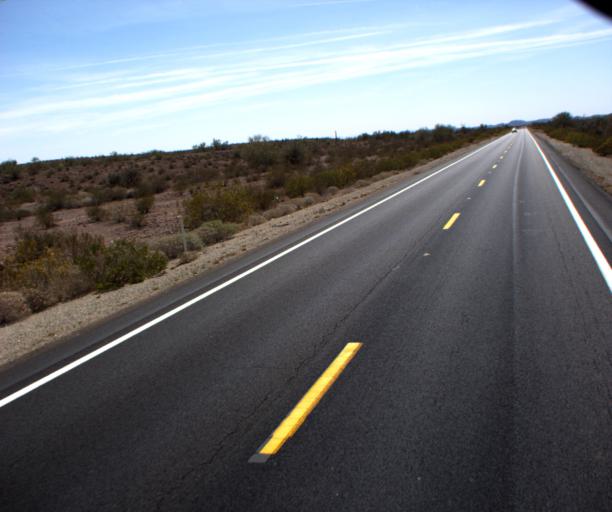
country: US
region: Arizona
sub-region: La Paz County
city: Quartzsite
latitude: 33.2147
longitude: -114.2616
